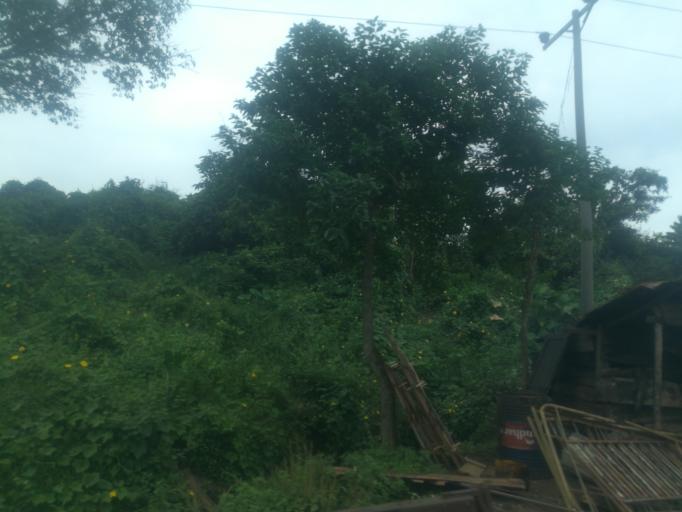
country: NG
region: Oyo
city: Ibadan
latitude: 7.3774
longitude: 3.9305
